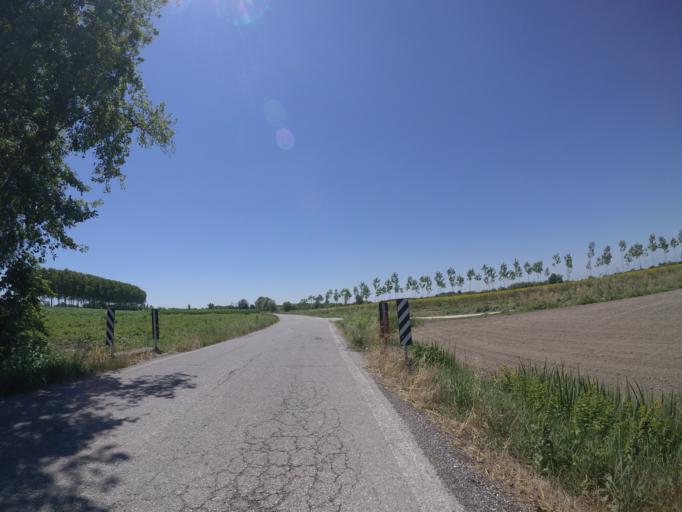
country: IT
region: Friuli Venezia Giulia
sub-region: Provincia di Udine
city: Teor
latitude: 45.8646
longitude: 13.0643
